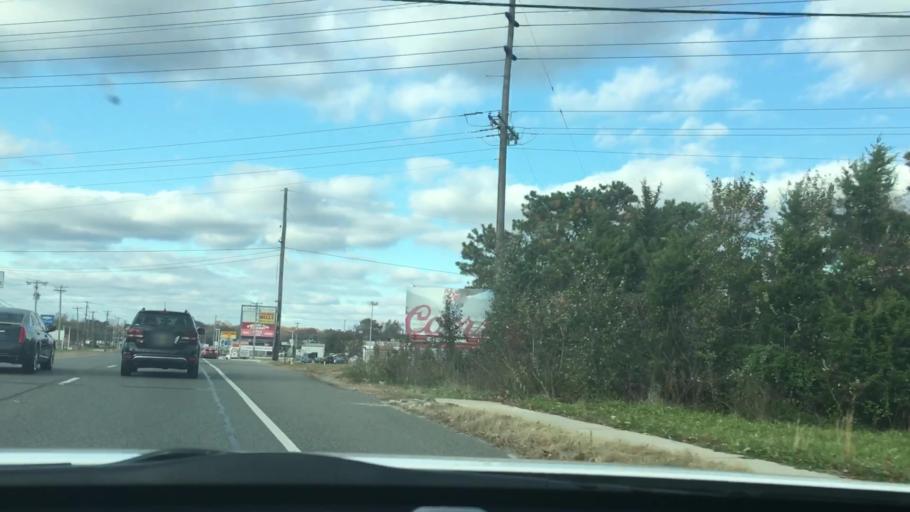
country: US
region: New Jersey
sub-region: Atlantic County
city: Northfield
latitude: 39.4027
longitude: -74.5622
